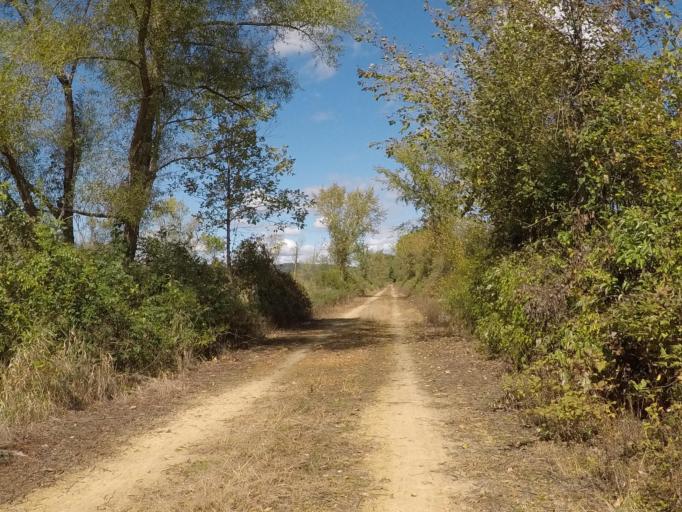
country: US
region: Wisconsin
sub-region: Richland County
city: Richland Center
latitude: 43.2408
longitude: -90.3026
